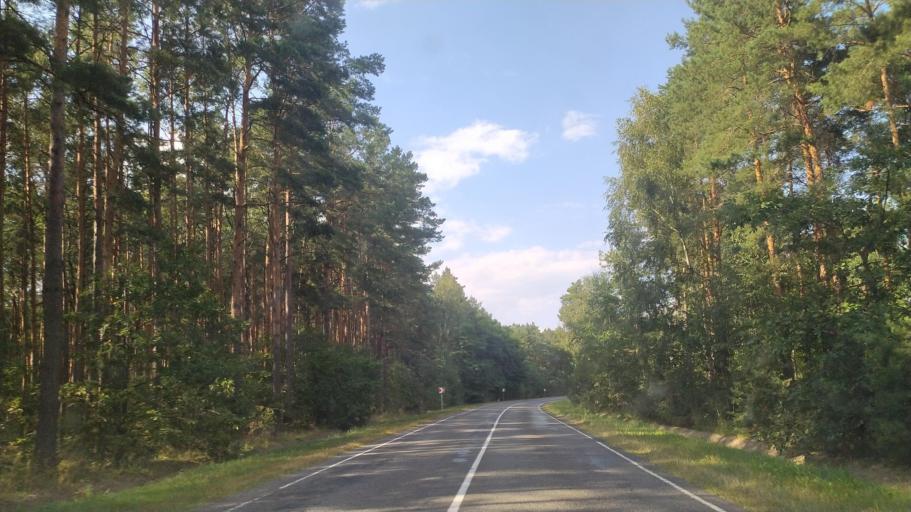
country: BY
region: Brest
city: Drahichyn
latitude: 52.3190
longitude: 25.0289
